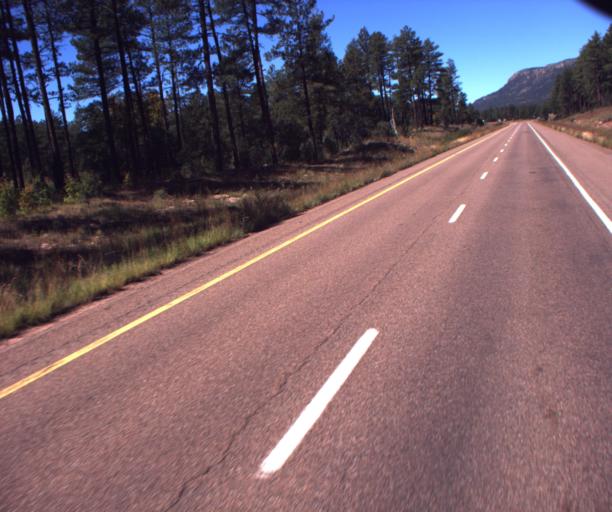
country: US
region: Arizona
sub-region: Gila County
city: Star Valley
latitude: 34.3038
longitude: -110.9915
